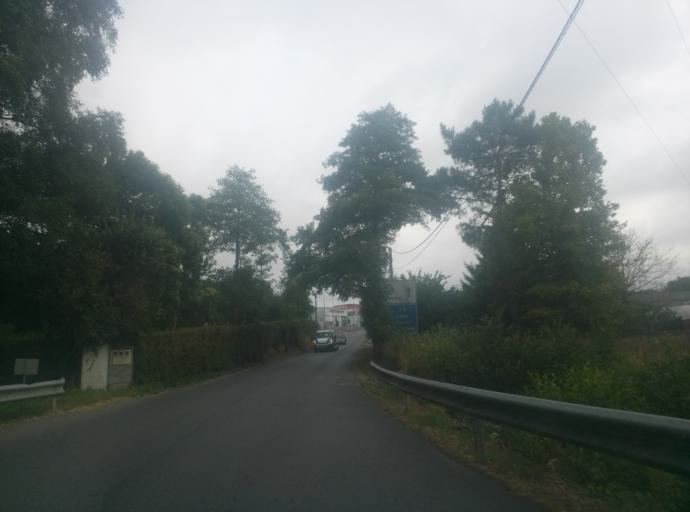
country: ES
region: Galicia
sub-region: Provincia de Lugo
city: Lugo
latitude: 43.0550
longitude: -7.5651
